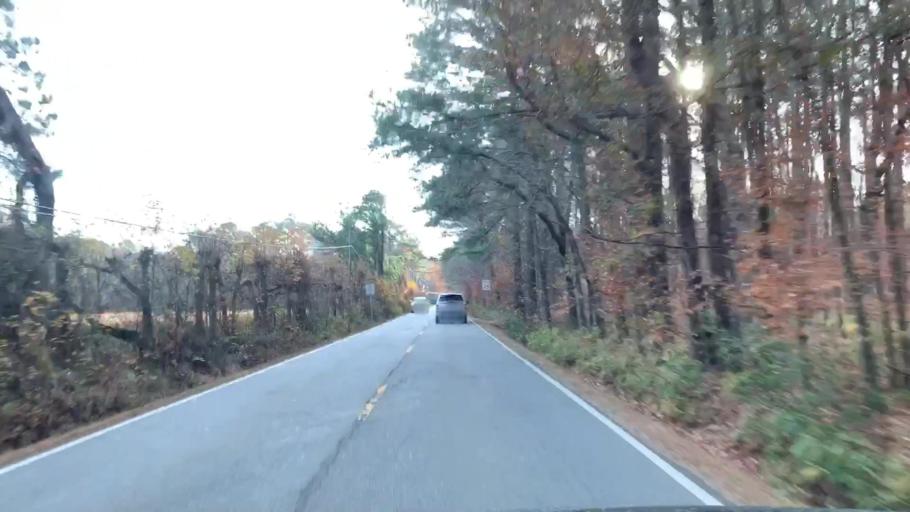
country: US
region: Virginia
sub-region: City of Virginia Beach
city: Virginia Beach
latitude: 36.7379
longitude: -76.1045
